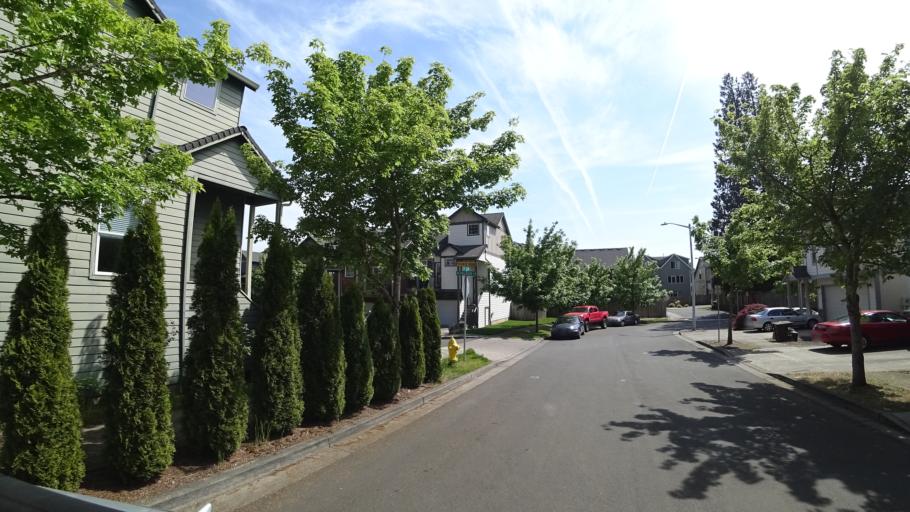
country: US
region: Oregon
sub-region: Washington County
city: Hillsboro
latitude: 45.5185
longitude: -122.9354
